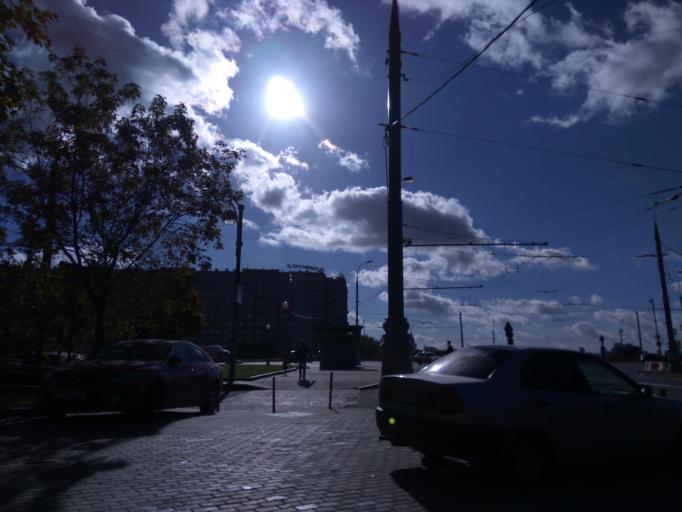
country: RU
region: Moskovskaya
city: Kastanayevo
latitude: 55.7372
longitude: 37.5164
